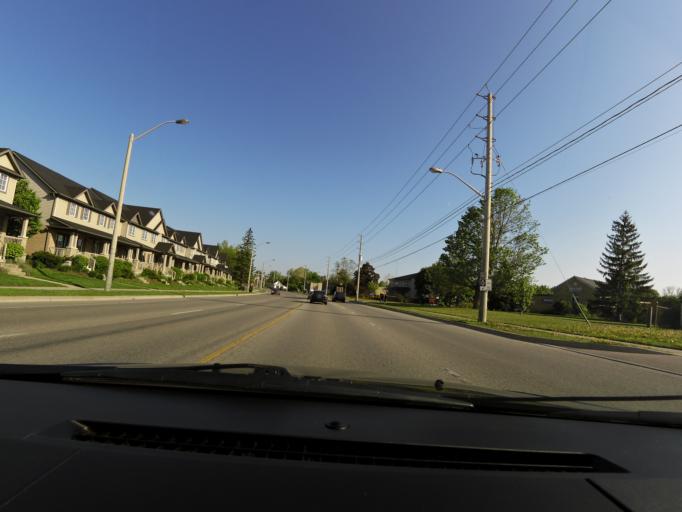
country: CA
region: Ontario
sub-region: Wellington County
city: Guelph
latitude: 43.5114
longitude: -80.1967
